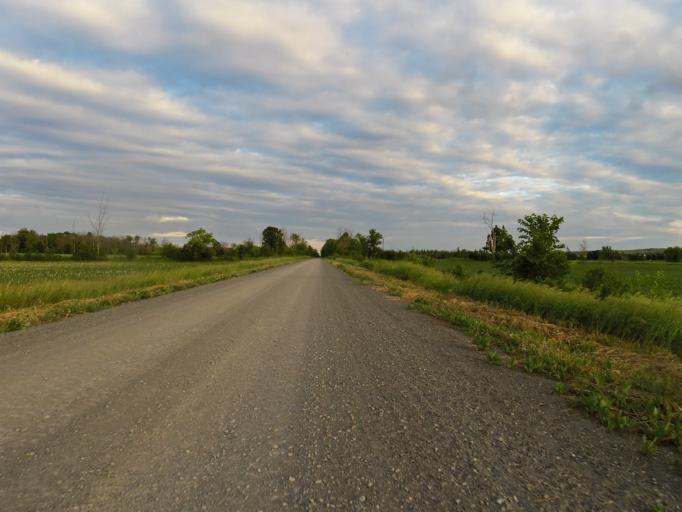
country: CA
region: Ontario
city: Arnprior
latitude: 45.3449
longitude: -76.3004
